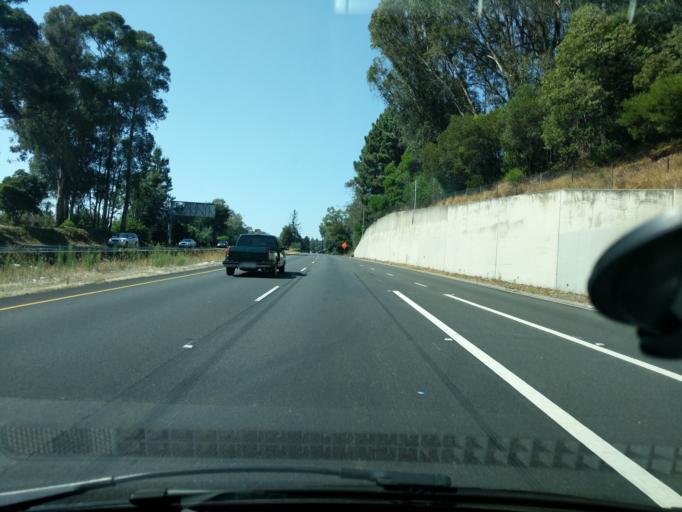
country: US
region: California
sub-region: Alameda County
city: Piedmont
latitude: 37.7999
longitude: -122.1863
